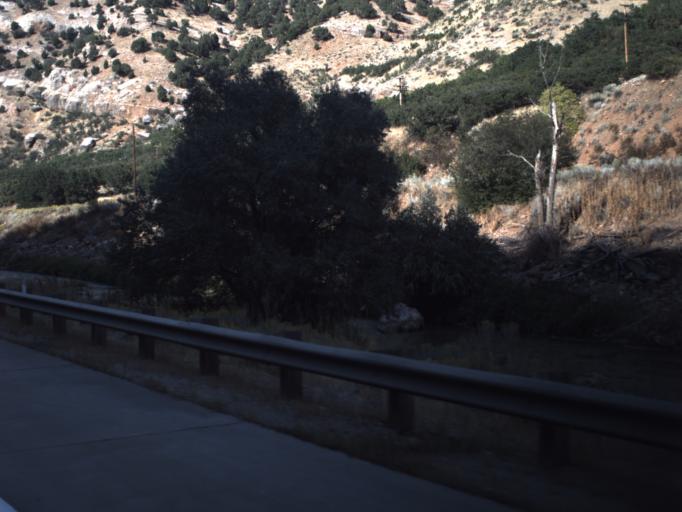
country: US
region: Utah
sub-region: Morgan County
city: Morgan
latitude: 41.0534
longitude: -111.5301
